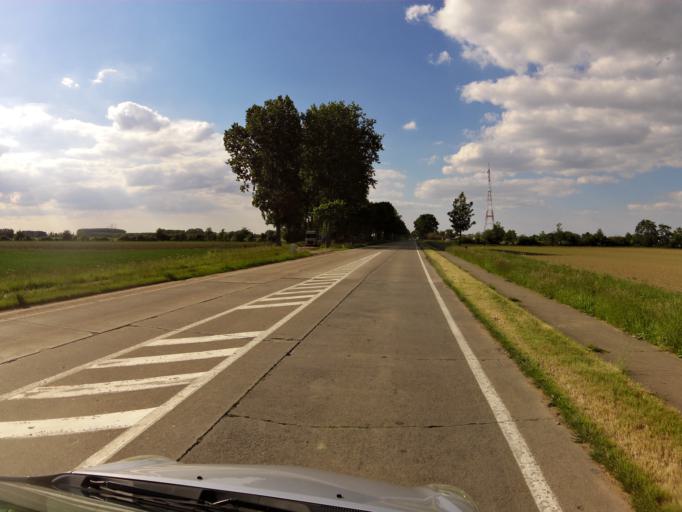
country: BE
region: Flanders
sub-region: Provincie West-Vlaanderen
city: Alveringem
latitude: 50.9367
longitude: 2.7322
